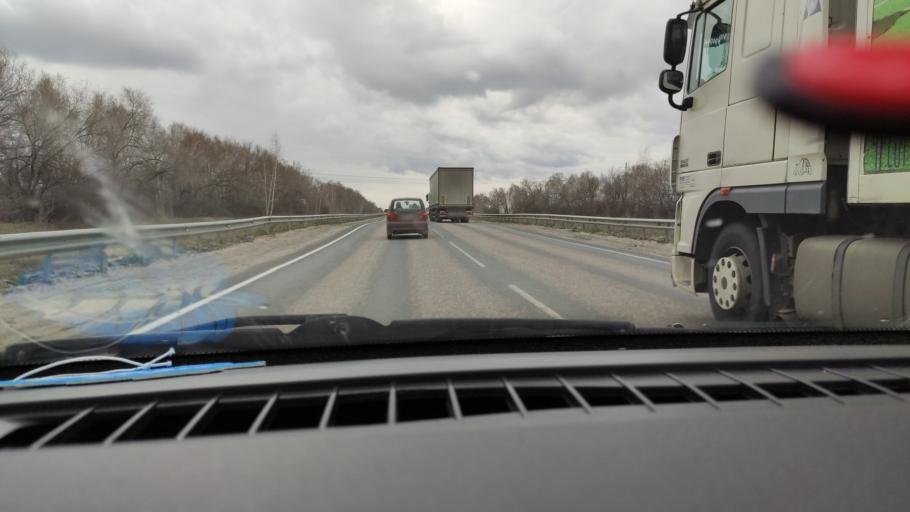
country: RU
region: Saratov
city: Sinodskoye
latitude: 51.9603
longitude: 46.6232
